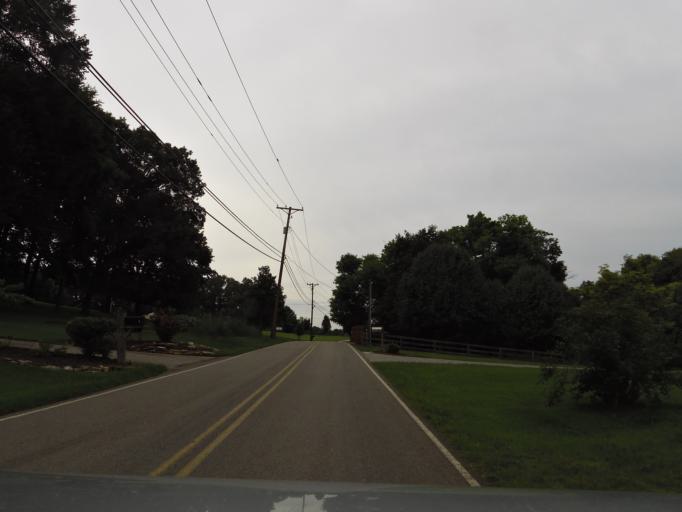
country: US
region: Tennessee
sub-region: Knox County
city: Knoxville
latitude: 35.8811
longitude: -83.9489
